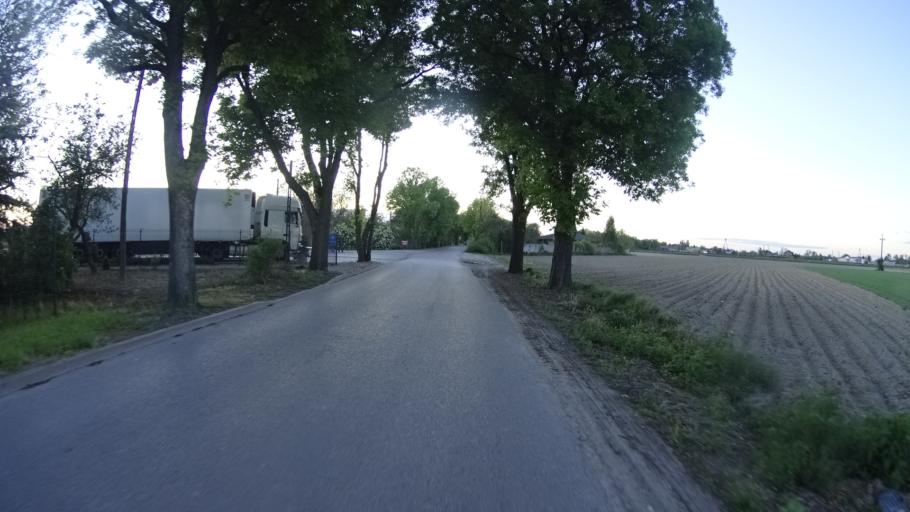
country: PL
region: Masovian Voivodeship
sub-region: Powiat warszawski zachodni
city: Ozarow Mazowiecki
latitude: 52.2053
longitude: 20.7568
